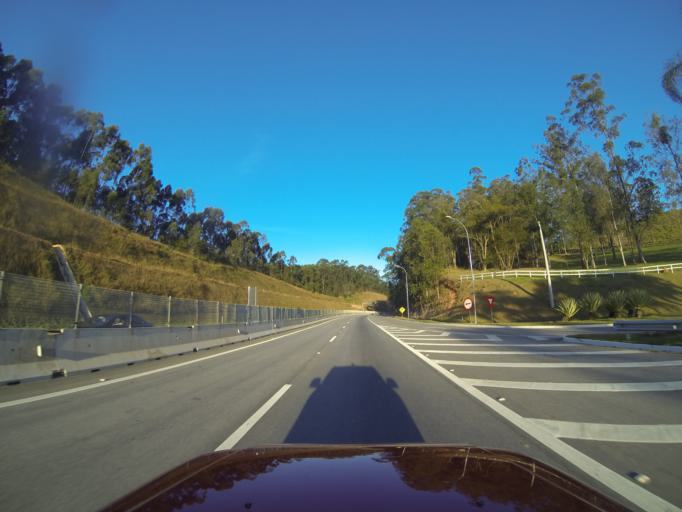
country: BR
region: Sao Paulo
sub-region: Caraguatatuba
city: Caraguatatuba
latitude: -23.4437
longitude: -45.6077
